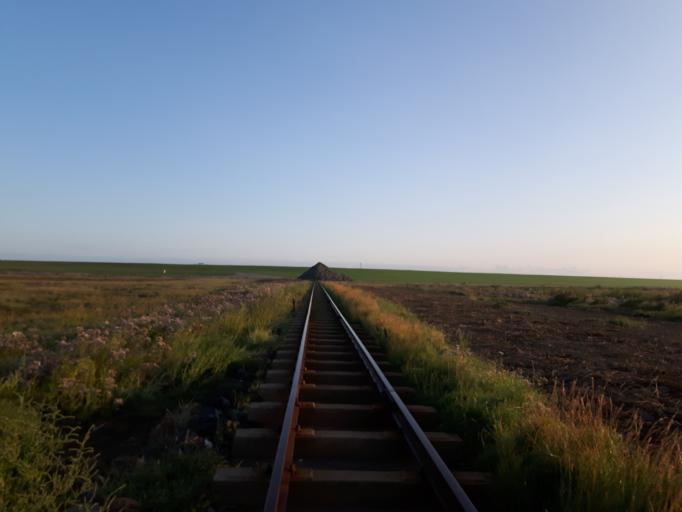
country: DE
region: Schleswig-Holstein
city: Dagebull
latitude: 54.7221
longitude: 8.7119
